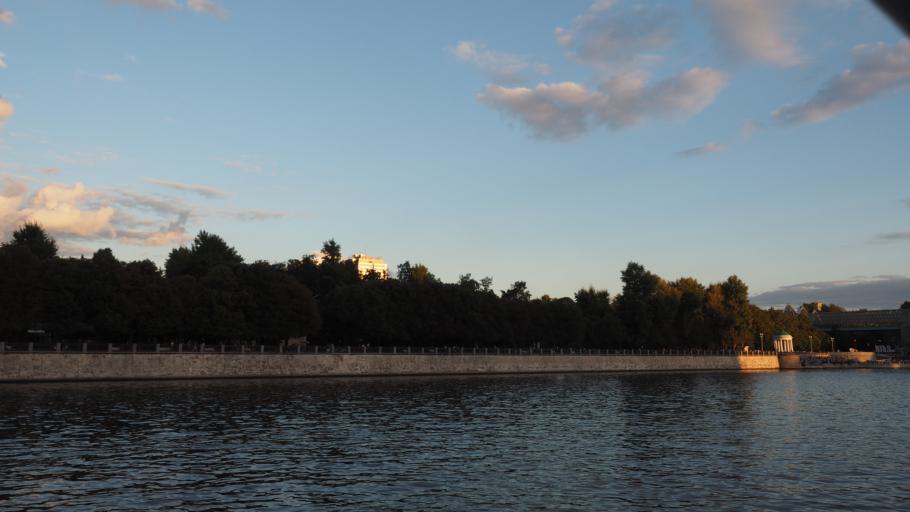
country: RU
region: Moscow
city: Novyye Cheremushki
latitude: 55.7277
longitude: 37.5940
